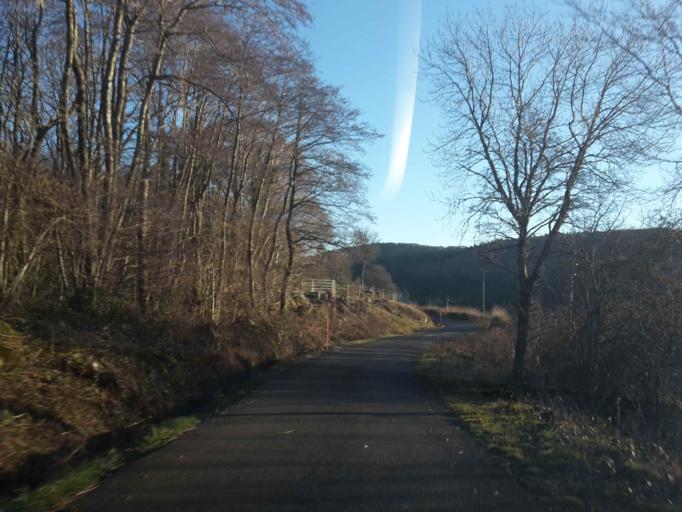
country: FR
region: Auvergne
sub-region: Departement du Cantal
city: Riom-es-Montagnes
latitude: 45.2284
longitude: 2.5641
